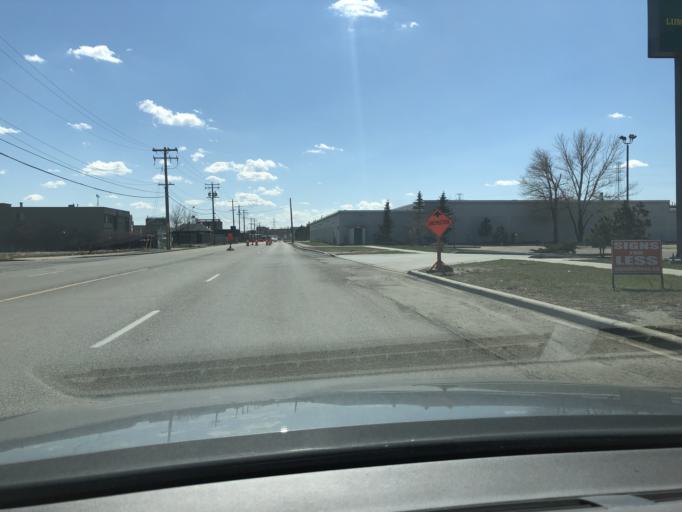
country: CA
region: Alberta
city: Calgary
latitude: 51.0287
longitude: -114.0310
